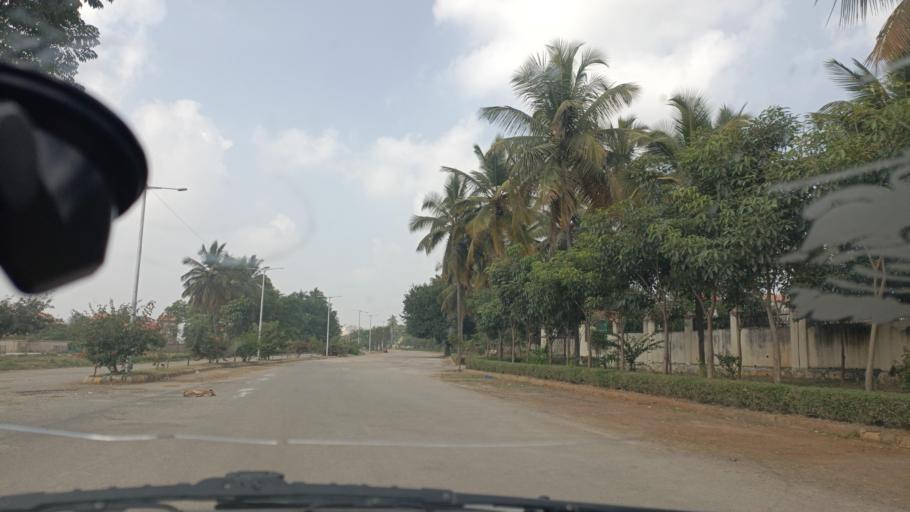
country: IN
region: Karnataka
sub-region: Bangalore Urban
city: Yelahanka
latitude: 13.1543
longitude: 77.6397
